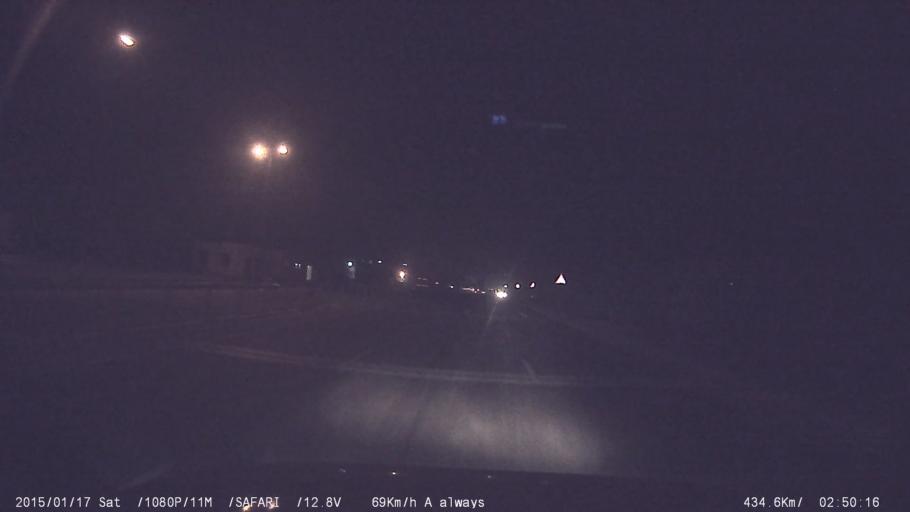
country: IN
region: Karnataka
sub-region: Bangalore Urban
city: Anekal
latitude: 12.8014
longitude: 77.7123
